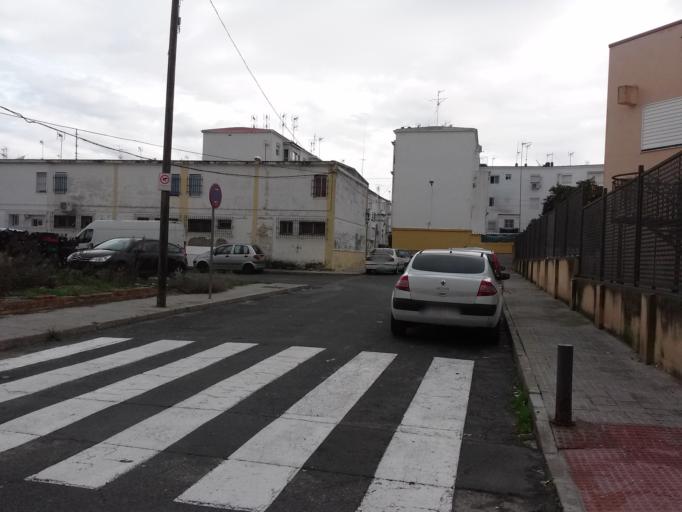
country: ES
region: Andalusia
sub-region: Provincia de Sevilla
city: Sevilla
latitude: 37.4266
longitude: -5.9844
